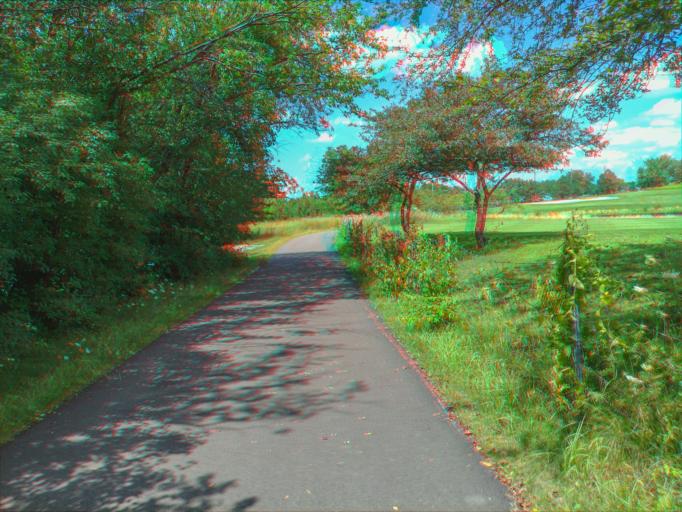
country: US
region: Illinois
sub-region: Lake County
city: Long Grove
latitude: 42.1459
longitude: -87.9996
